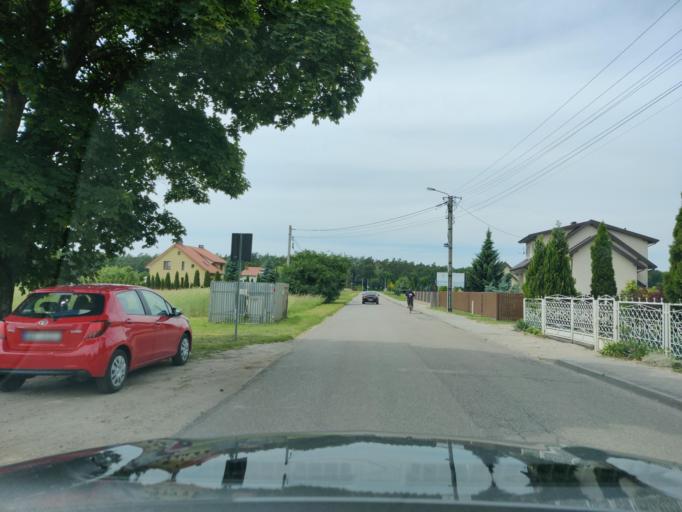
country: PL
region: Masovian Voivodeship
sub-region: Powiat wyszkowski
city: Rzasnik
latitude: 52.6988
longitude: 21.4034
